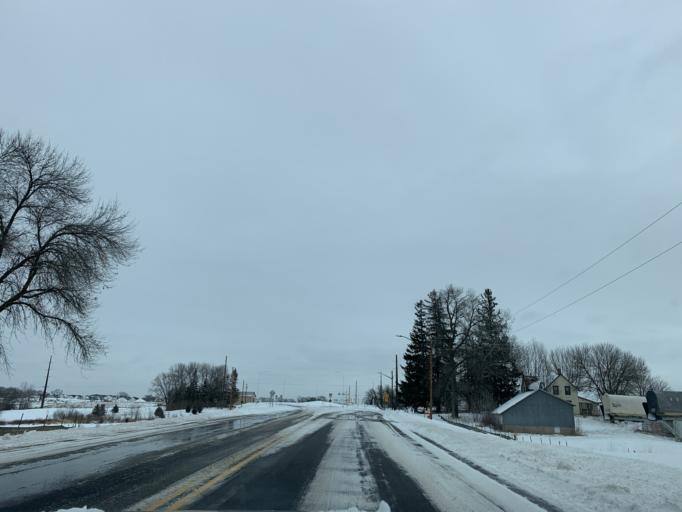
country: US
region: Minnesota
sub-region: Carver County
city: Carver
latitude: 44.7911
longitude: -93.6370
